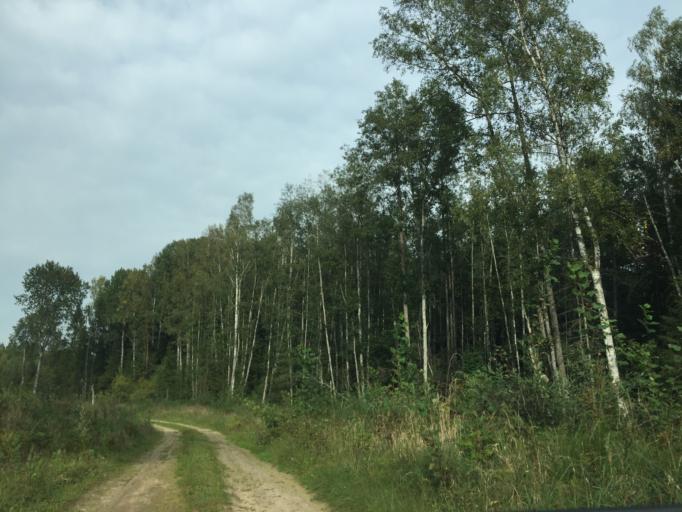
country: LV
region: Ikskile
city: Ikskile
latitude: 56.7578
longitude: 24.4744
